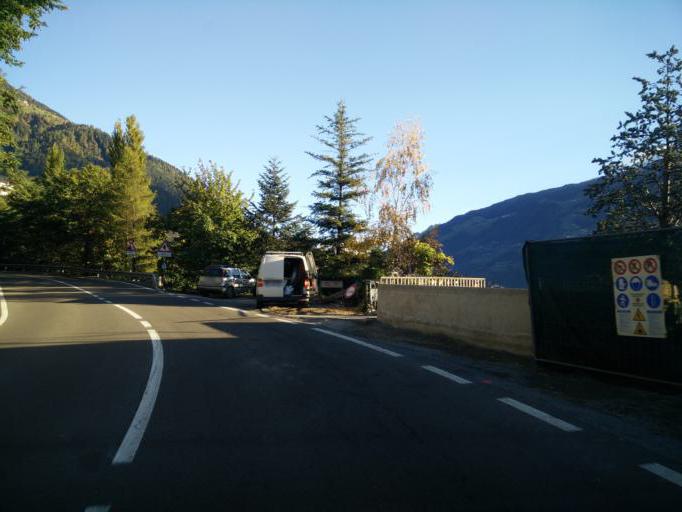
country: IT
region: Trentino-Alto Adige
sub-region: Bolzano
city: Caines
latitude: 46.6917
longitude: 11.1712
